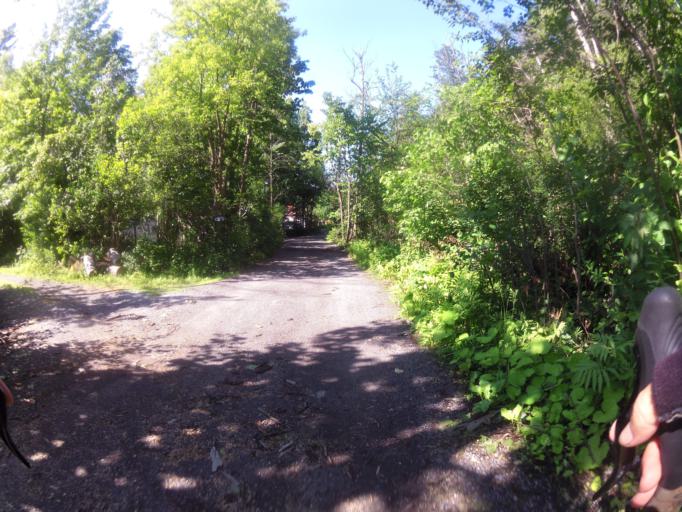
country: CA
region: Ontario
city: Ottawa
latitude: 45.3299
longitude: -75.6977
